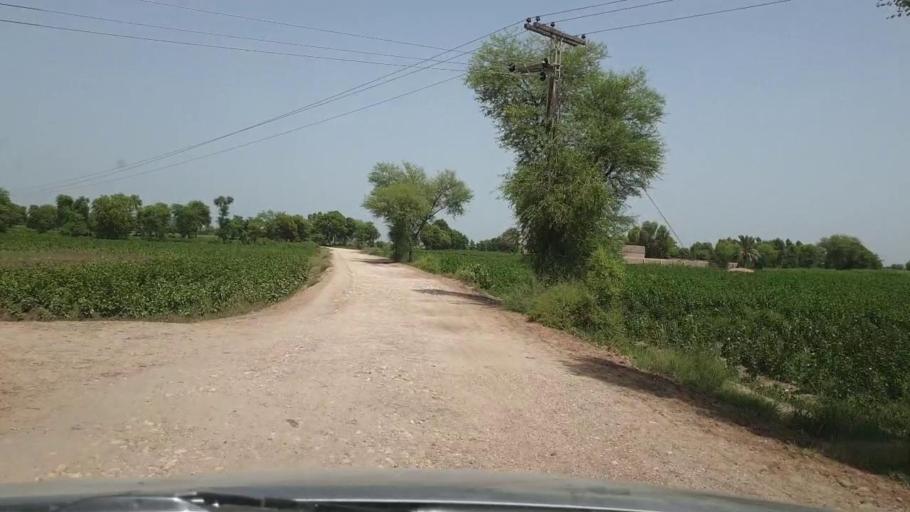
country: PK
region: Sindh
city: Pano Aqil
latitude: 27.8071
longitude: 69.2308
